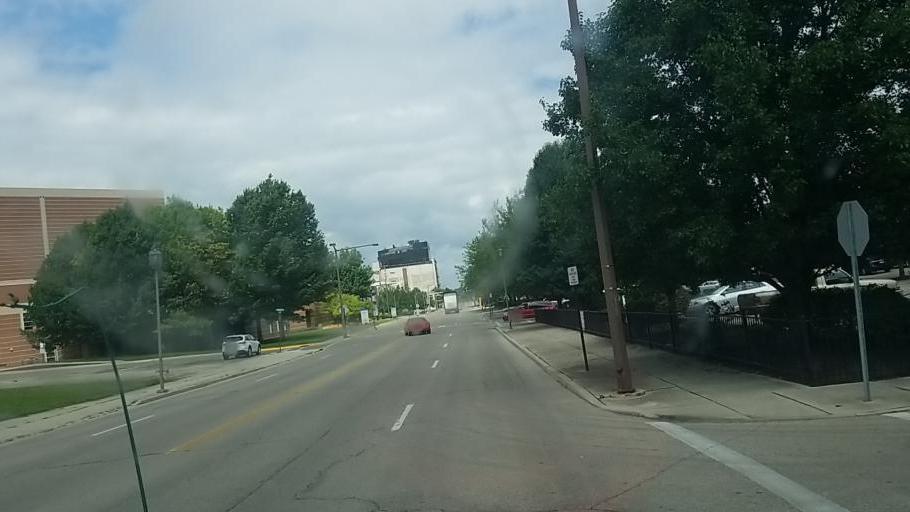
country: US
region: Ohio
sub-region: Clark County
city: Springfield
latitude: 39.9197
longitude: -83.8089
